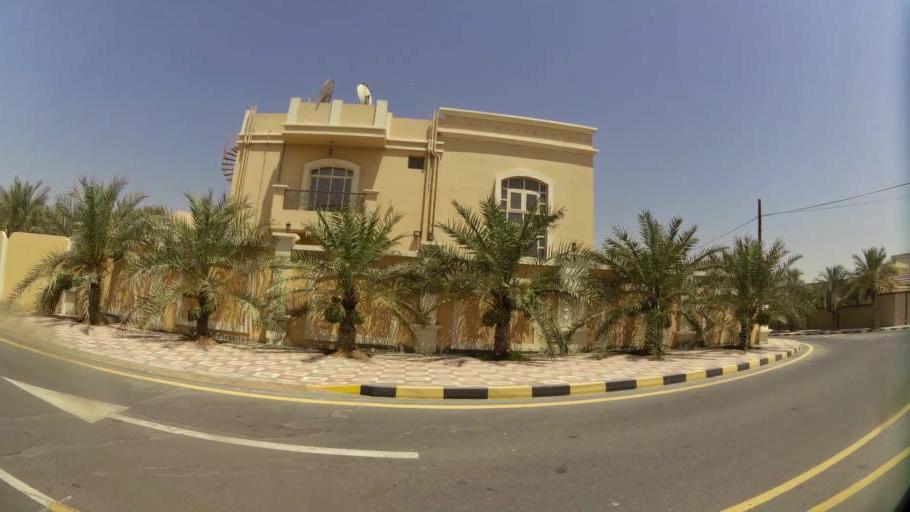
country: AE
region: Ajman
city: Ajman
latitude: 25.4008
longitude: 55.5173
